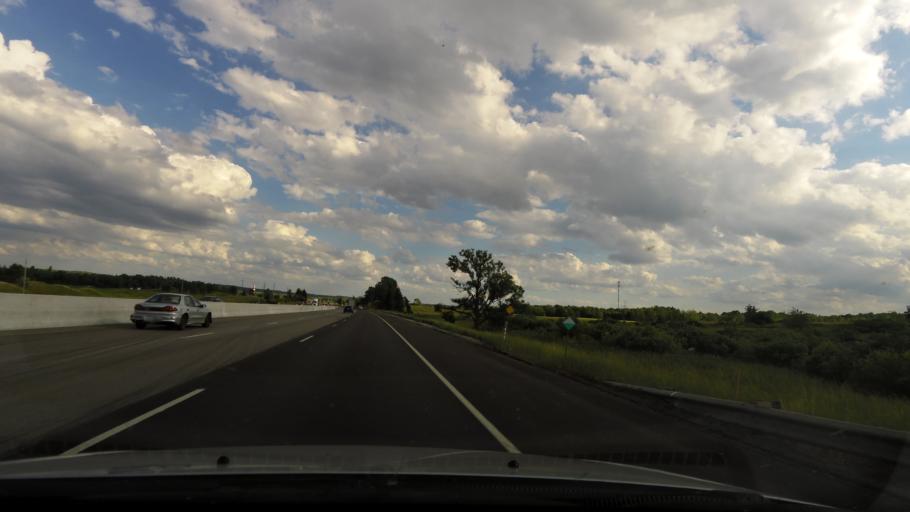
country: CA
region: Ontario
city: Innisfil
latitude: 44.2116
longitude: -79.6601
